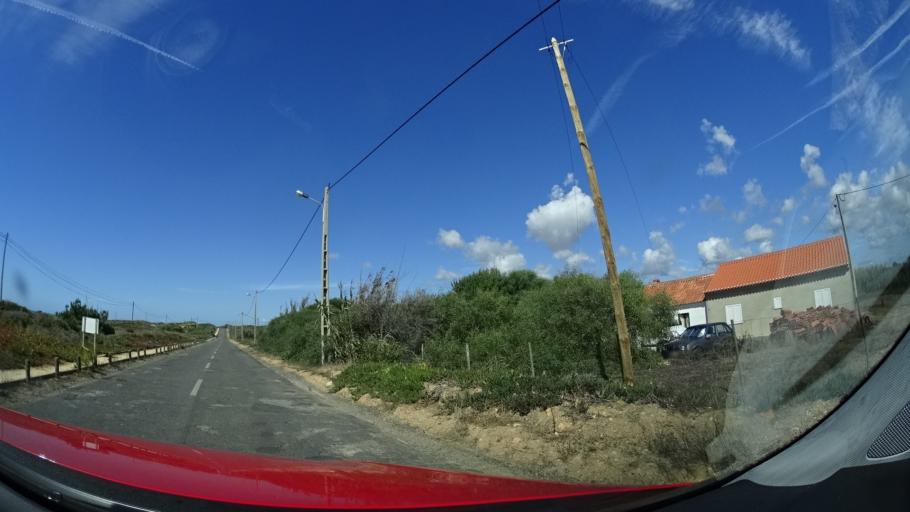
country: PT
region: Beja
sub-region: Odemira
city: Sao Teotonio
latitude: 37.5294
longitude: -8.7843
